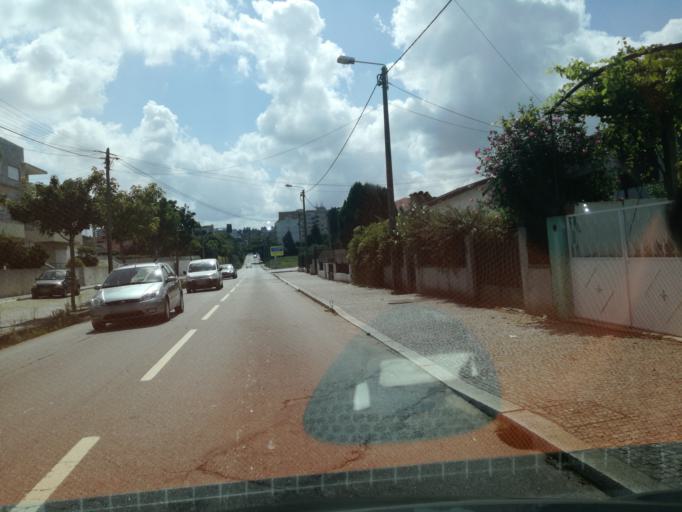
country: PT
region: Porto
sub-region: Maia
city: Nogueira
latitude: 41.2323
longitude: -8.5919
